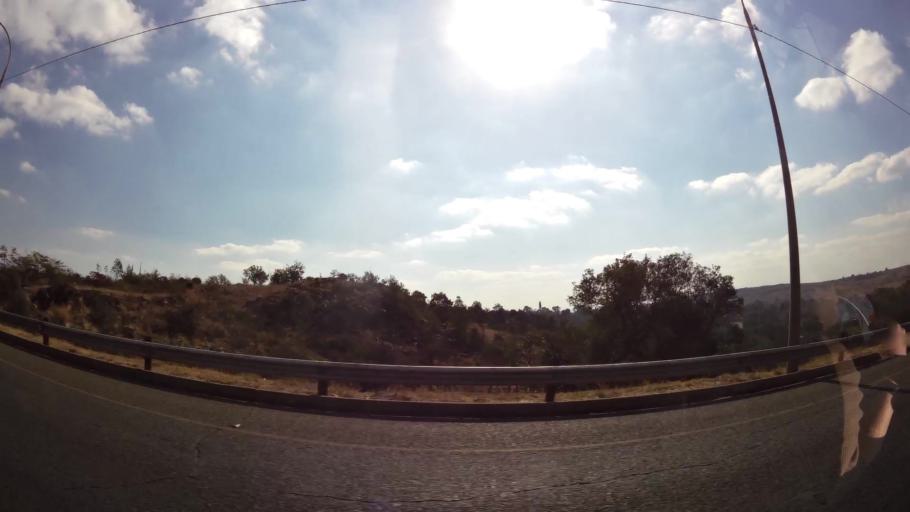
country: ZA
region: Gauteng
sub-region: West Rand District Municipality
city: Krugersdorp
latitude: -26.0746
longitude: 27.7983
